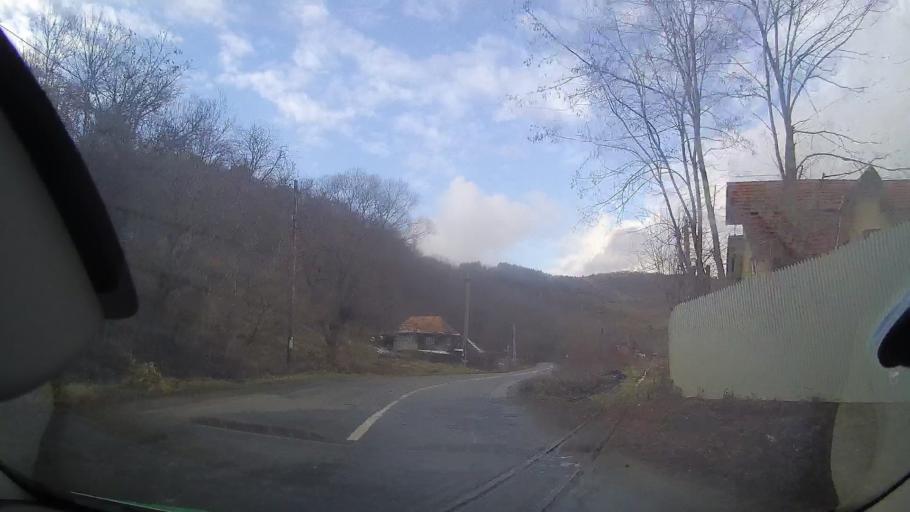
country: RO
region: Alba
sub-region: Comuna Ocolis
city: Ocolis
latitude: 46.4343
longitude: 23.4570
